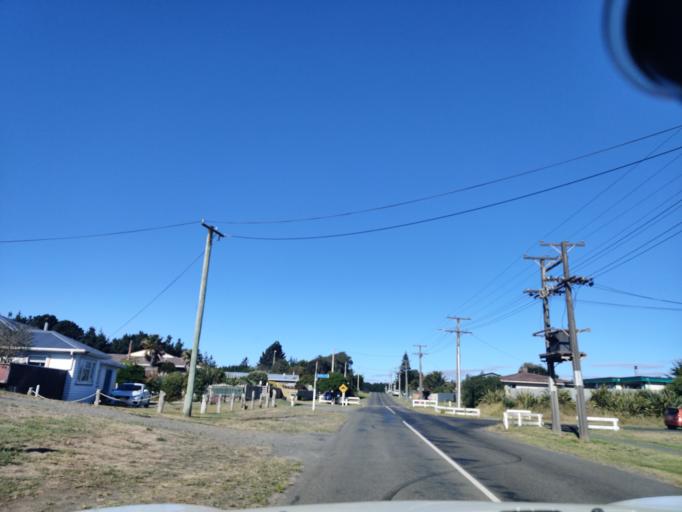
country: NZ
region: Manawatu-Wanganui
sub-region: Horowhenua District
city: Foxton
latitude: -40.3701
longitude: 175.2387
